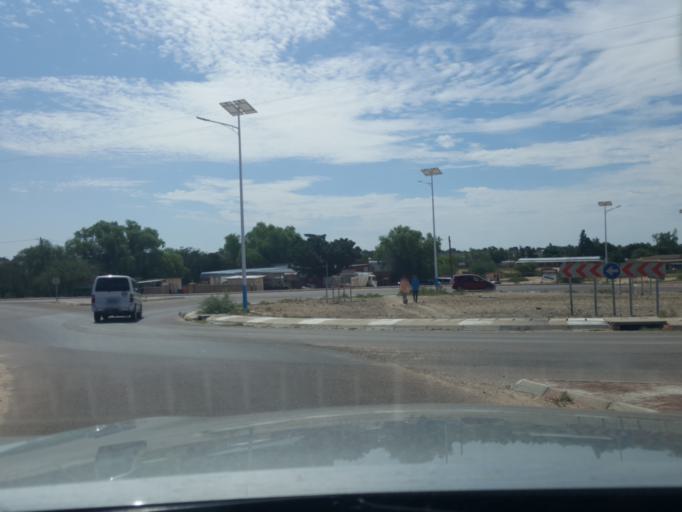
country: BW
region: Kweneng
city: Letlhakeng
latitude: -24.1003
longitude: 25.0296
